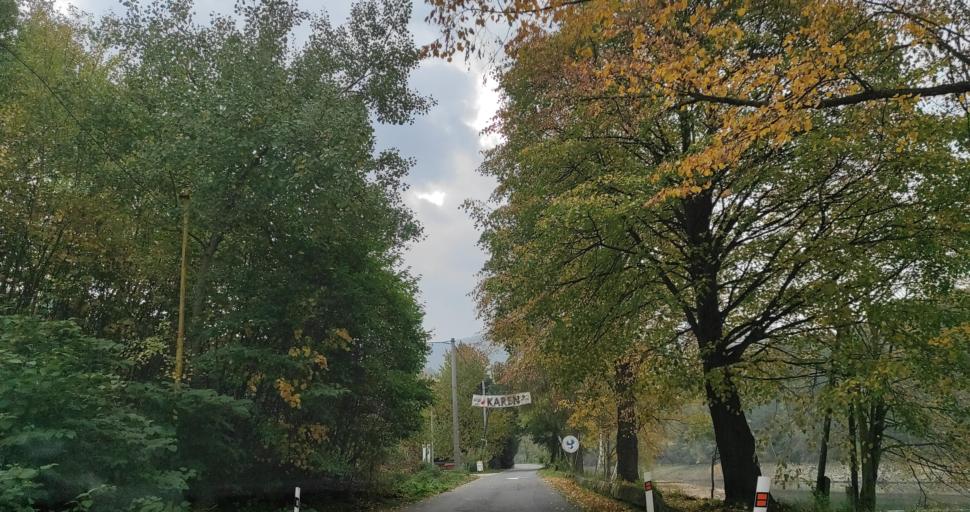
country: SK
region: Kosicky
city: Gelnica
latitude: 48.8899
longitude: 21.0385
